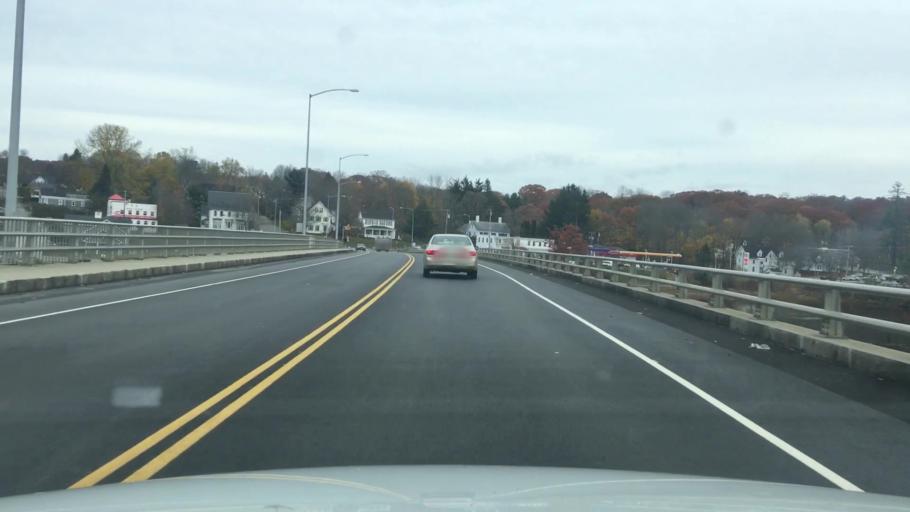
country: US
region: Maine
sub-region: Hancock County
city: Bucksport
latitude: 44.5689
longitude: -68.7885
